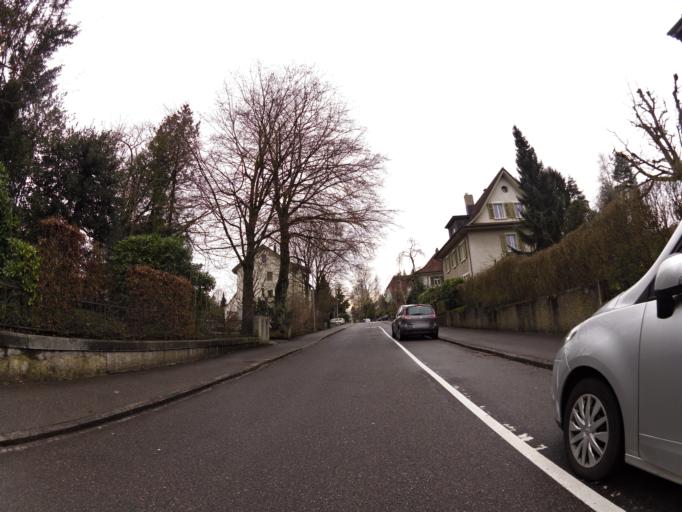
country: CH
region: Aargau
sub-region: Bezirk Aarau
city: Aarau
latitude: 47.3864
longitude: 8.0486
